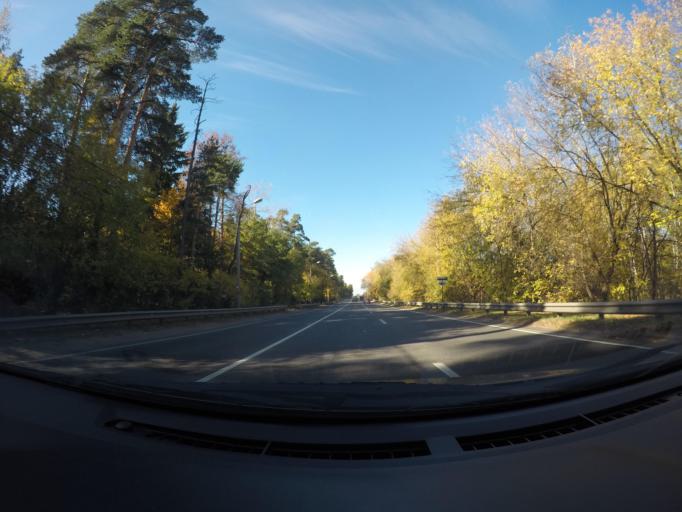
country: RU
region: Moskovskaya
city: Udel'naya
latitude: 55.6290
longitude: 37.9907
